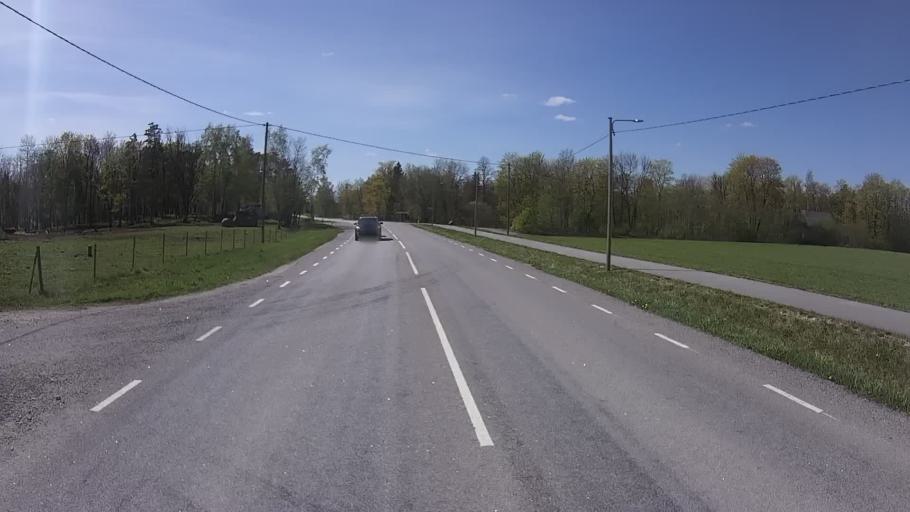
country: EE
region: Laeaene
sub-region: Ridala Parish
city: Uuemoisa
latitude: 58.9915
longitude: 23.7014
